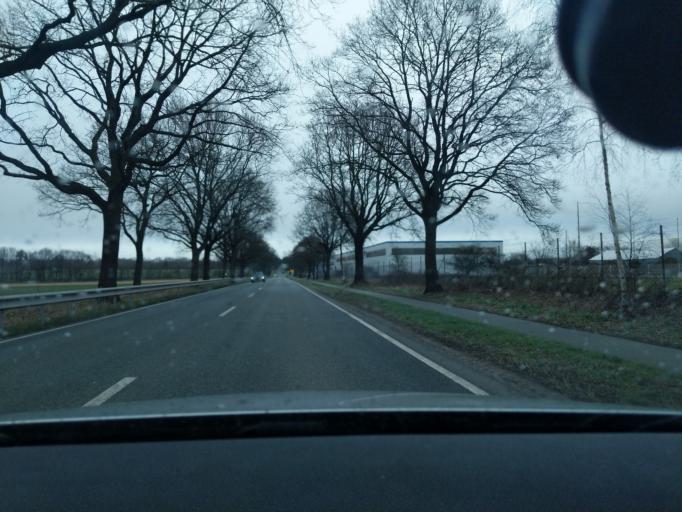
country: DE
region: Lower Saxony
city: Dudenbuttel
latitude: 53.5782
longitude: 9.4018
